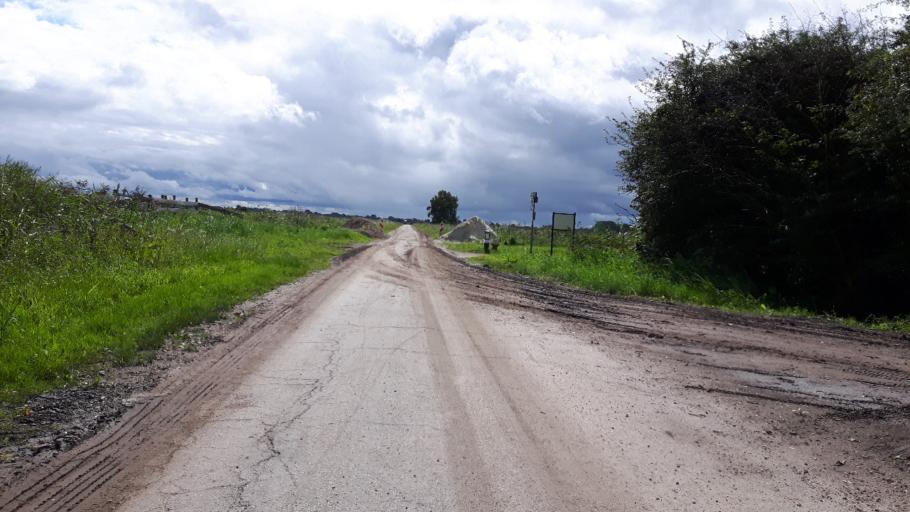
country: NL
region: Groningen
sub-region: Gemeente Slochteren
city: Slochteren
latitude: 53.2636
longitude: 6.8056
